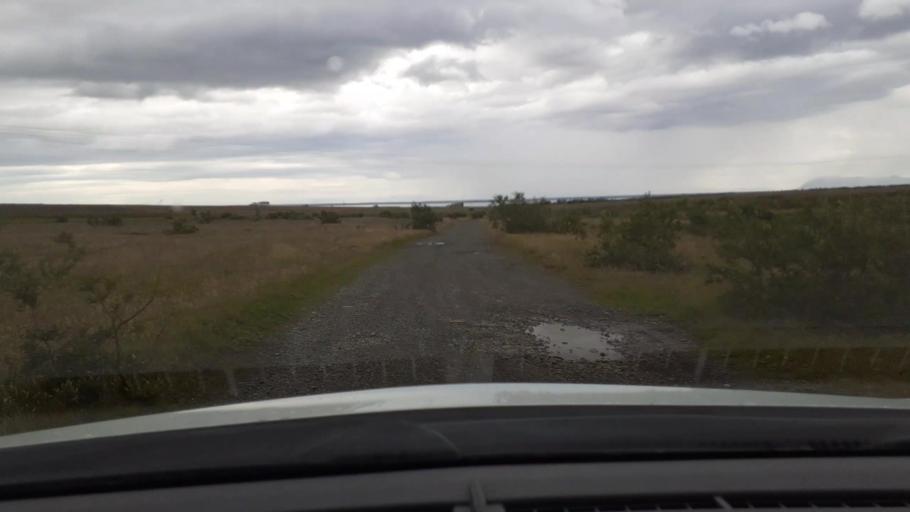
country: IS
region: West
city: Borgarnes
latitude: 64.4614
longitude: -21.9558
